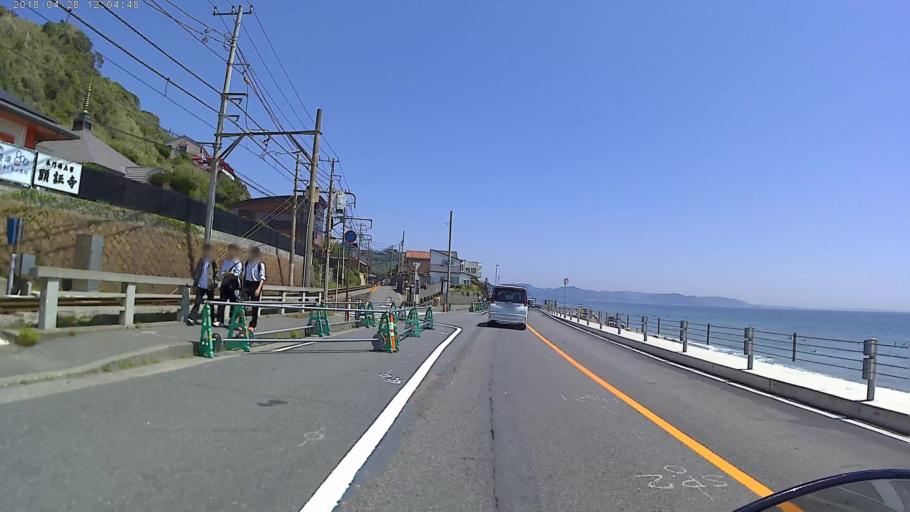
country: JP
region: Kanagawa
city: Kamakura
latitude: 35.3061
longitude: 139.5060
